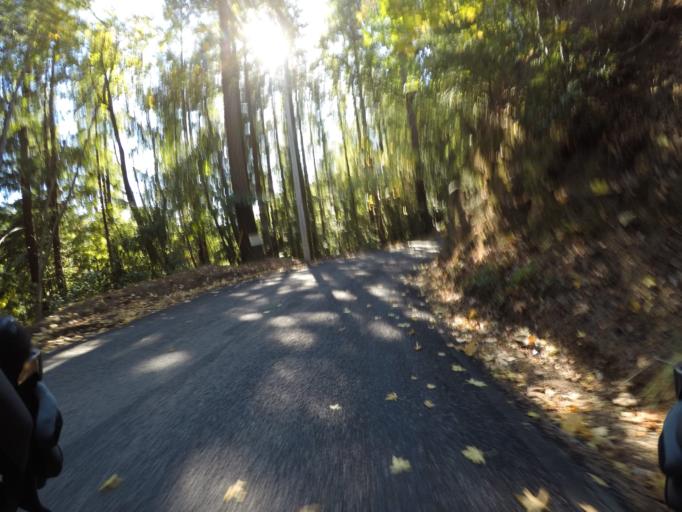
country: US
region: California
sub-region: Santa Cruz County
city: Lompico
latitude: 37.1291
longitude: -122.0176
